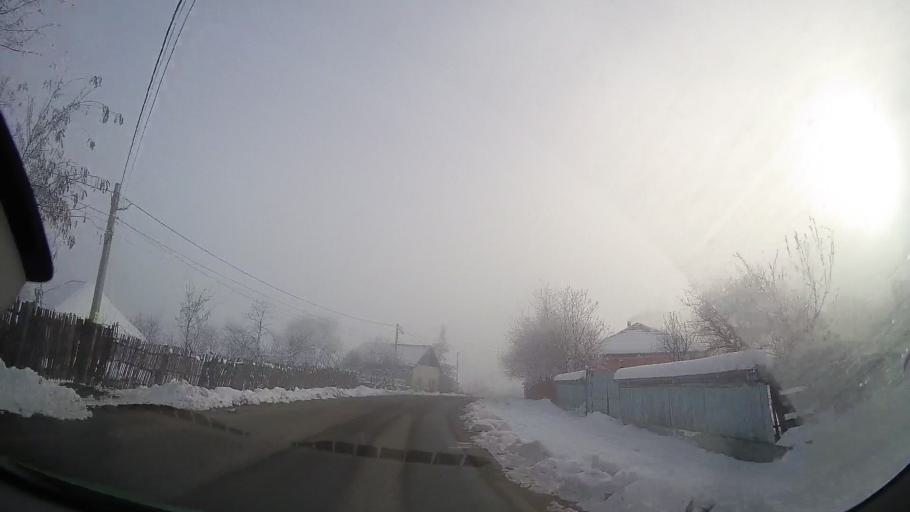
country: RO
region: Iasi
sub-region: Comuna Valea Seaca
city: Topile
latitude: 47.2462
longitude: 26.6630
